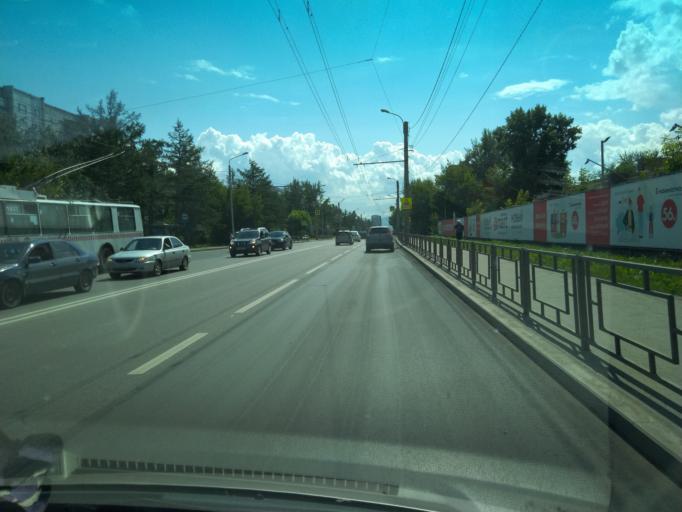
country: RU
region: Krasnoyarskiy
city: Solnechnyy
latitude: 56.0532
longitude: 92.9412
